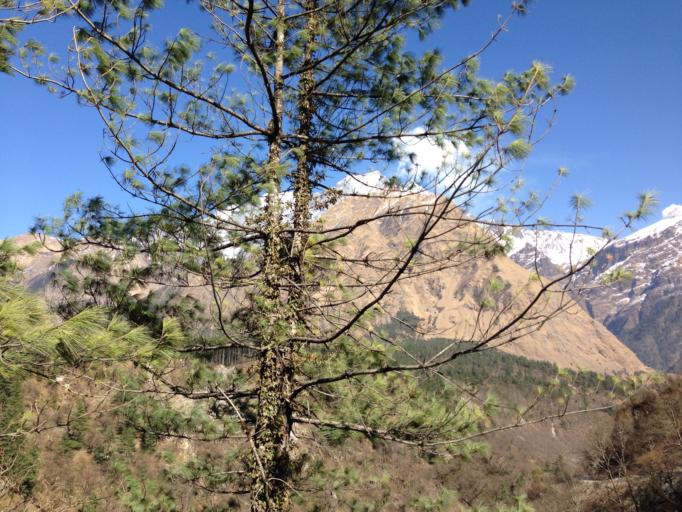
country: NP
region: Western Region
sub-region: Dhawalagiri Zone
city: Jomsom
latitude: 28.6269
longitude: 83.6169
